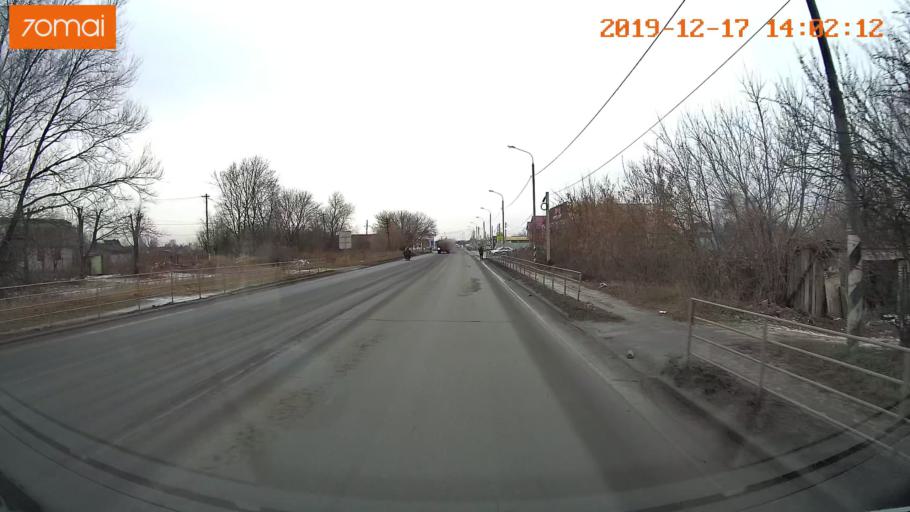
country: RU
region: Rjazan
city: Ryazan'
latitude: 54.6155
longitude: 39.6494
